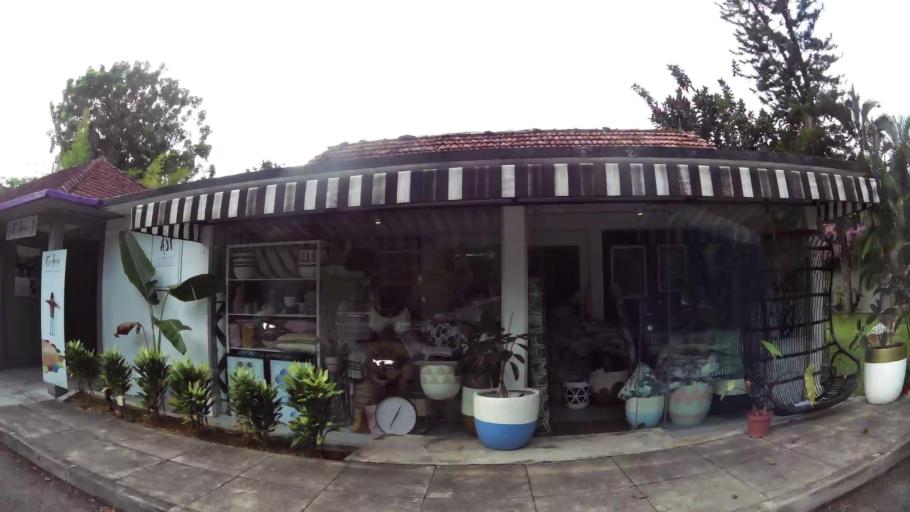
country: SG
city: Singapore
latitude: 1.3050
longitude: 103.8084
